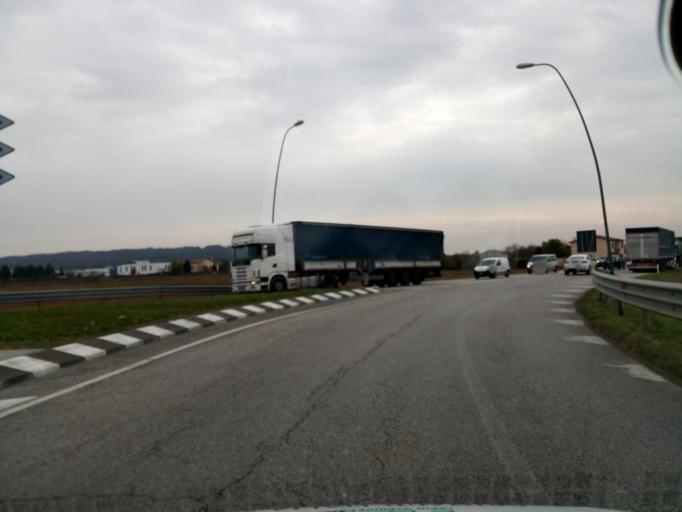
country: IT
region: Veneto
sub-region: Provincia di Treviso
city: Crocetta-Nogare
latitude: 45.8135
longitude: 12.0158
